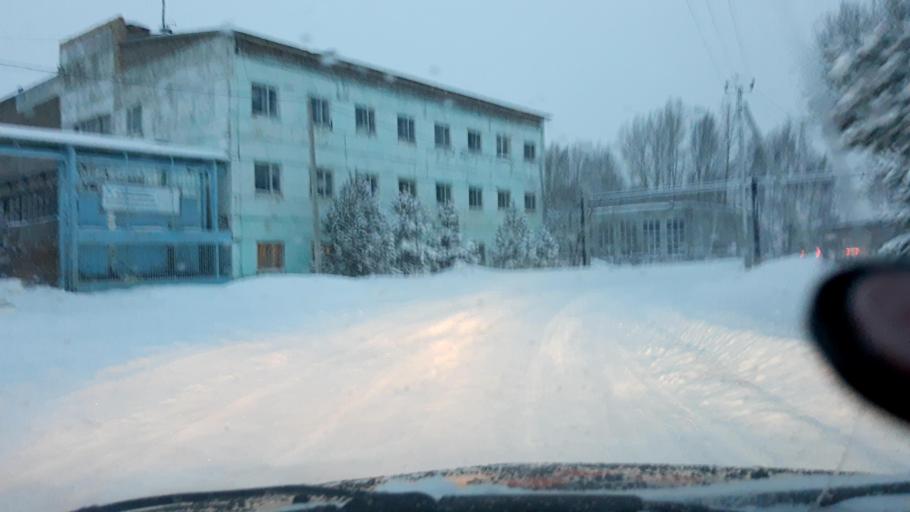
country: RU
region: Bashkortostan
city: Blagoveshchensk
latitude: 55.0300
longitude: 56.0189
